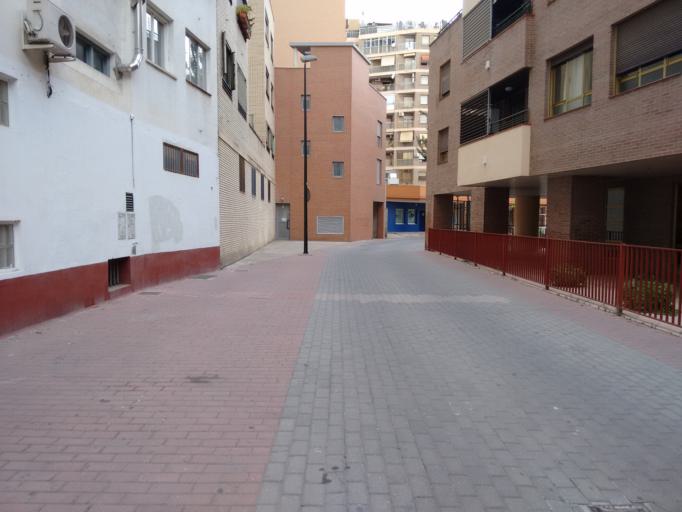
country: ES
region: Aragon
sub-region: Provincia de Zaragoza
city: Zaragoza
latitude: 41.6384
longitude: -0.8780
